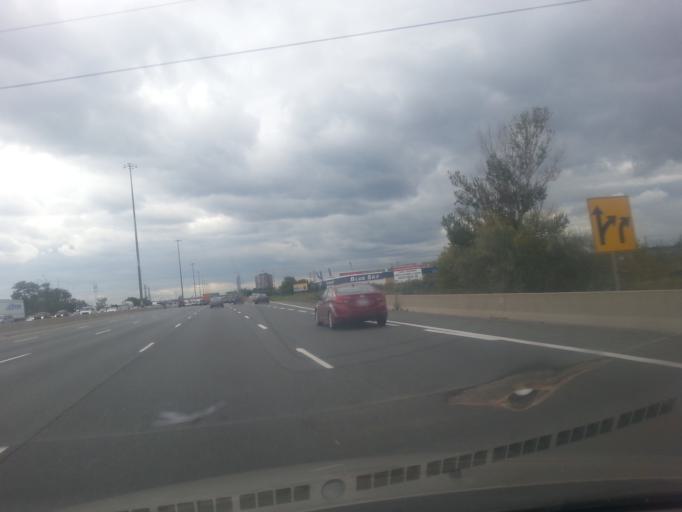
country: CA
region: Ontario
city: Ajax
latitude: 43.8433
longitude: -79.0613
